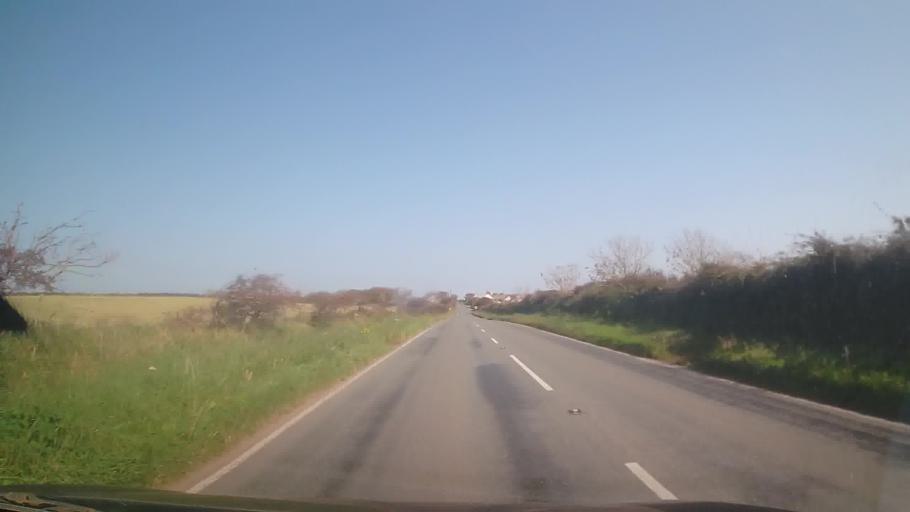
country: GB
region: Wales
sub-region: Pembrokeshire
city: Llanrhian
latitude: 51.9311
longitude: -5.1506
